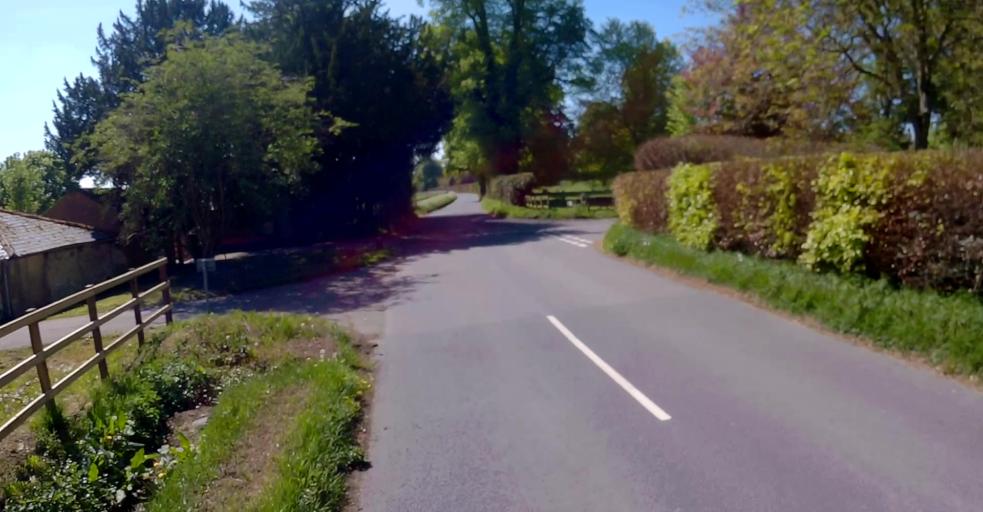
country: GB
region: England
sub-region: Hampshire
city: Andover
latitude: 51.1933
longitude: -1.3935
